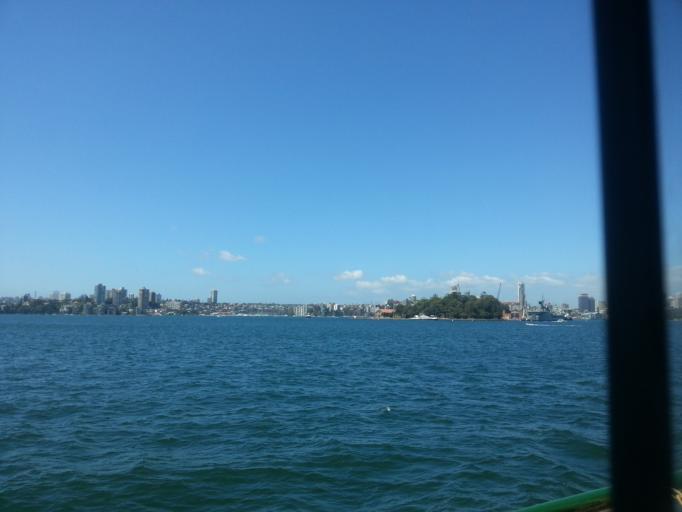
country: AU
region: New South Wales
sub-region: North Sydney
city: Cremorne Point
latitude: -33.8521
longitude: 151.2318
